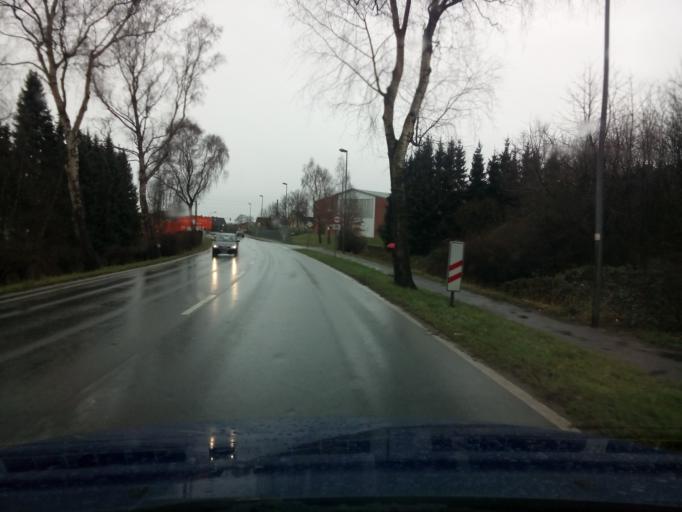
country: DE
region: Lower Saxony
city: Ritterhude
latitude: 53.1887
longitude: 8.7560
